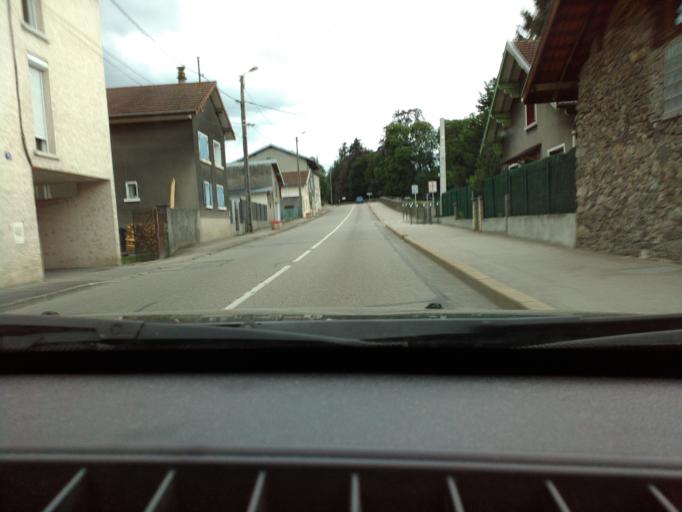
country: FR
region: Rhone-Alpes
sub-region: Departement de l'Isere
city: Villard-Bonnot
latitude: 45.2484
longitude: 5.8975
